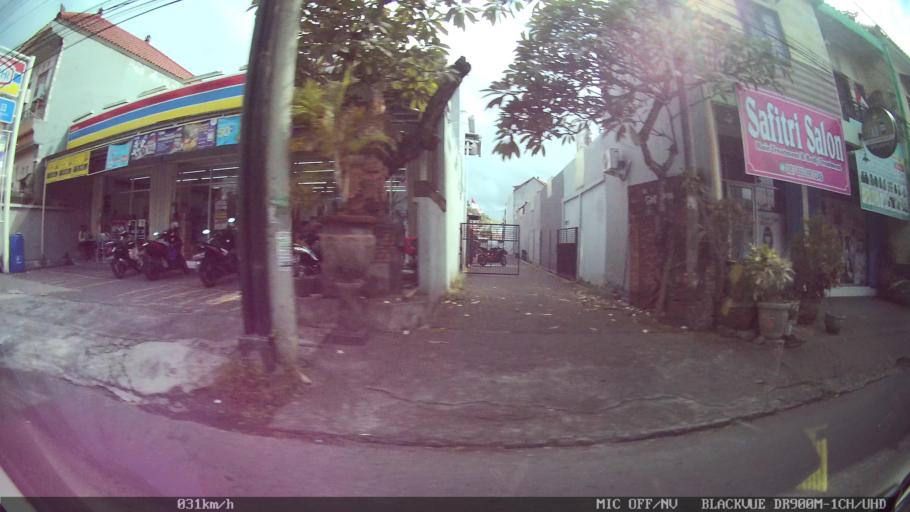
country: ID
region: Bali
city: Banjar Kertasari
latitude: -8.6202
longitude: 115.2043
